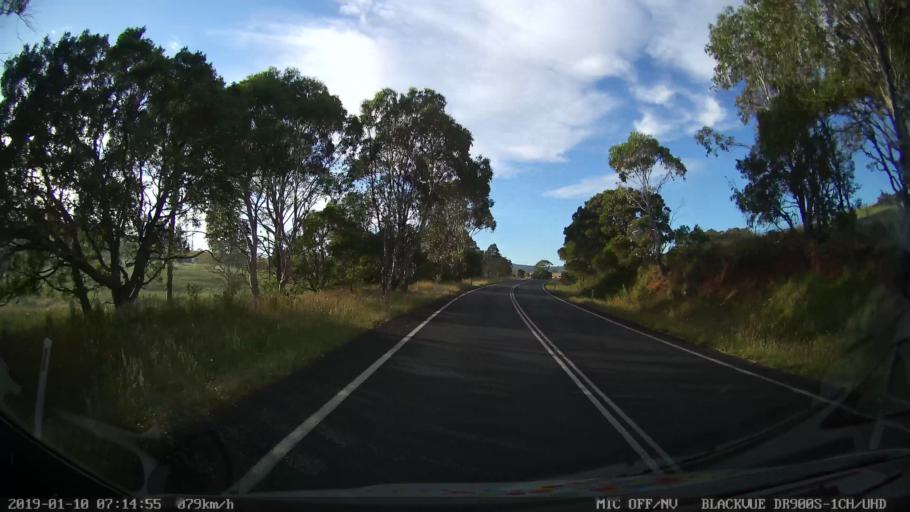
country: AU
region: New South Wales
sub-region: Bellingen
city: Dorrigo
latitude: -30.3588
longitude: 152.4902
